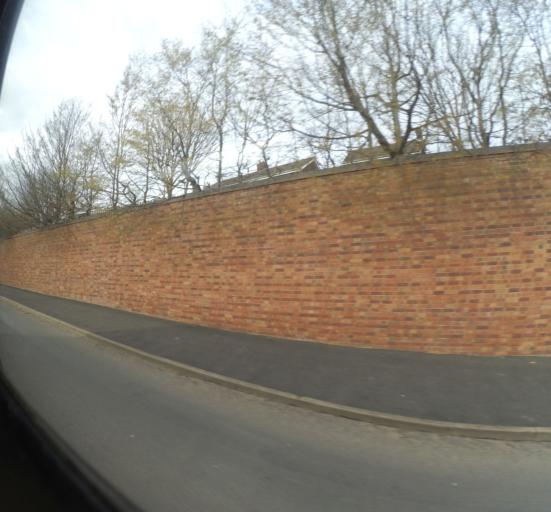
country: GB
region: England
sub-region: Warwickshire
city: Long Lawford
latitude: 52.3907
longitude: -1.2825
